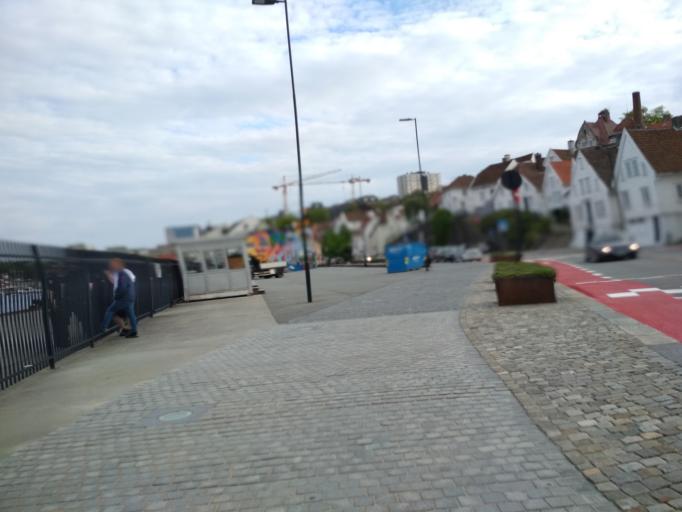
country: NO
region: Rogaland
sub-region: Stavanger
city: Stavanger
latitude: 58.9738
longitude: 5.7259
